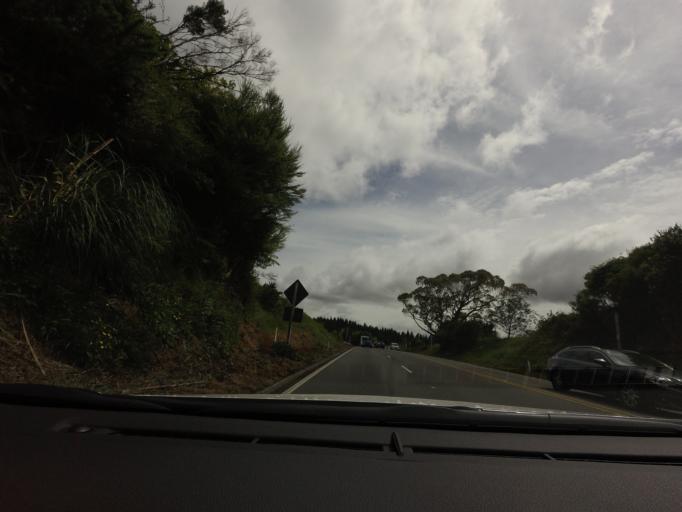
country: NZ
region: Auckland
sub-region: Auckland
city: Warkworth
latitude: -36.4791
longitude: 174.6570
